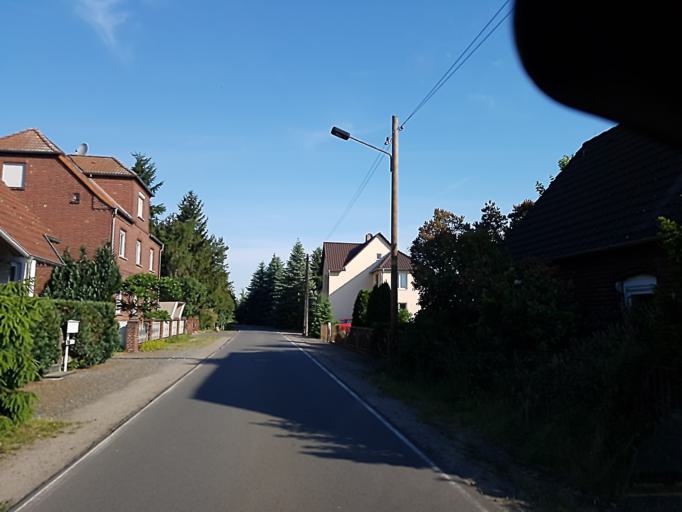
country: DE
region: Saxony-Anhalt
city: Abtsdorf
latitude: 51.8673
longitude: 12.7050
